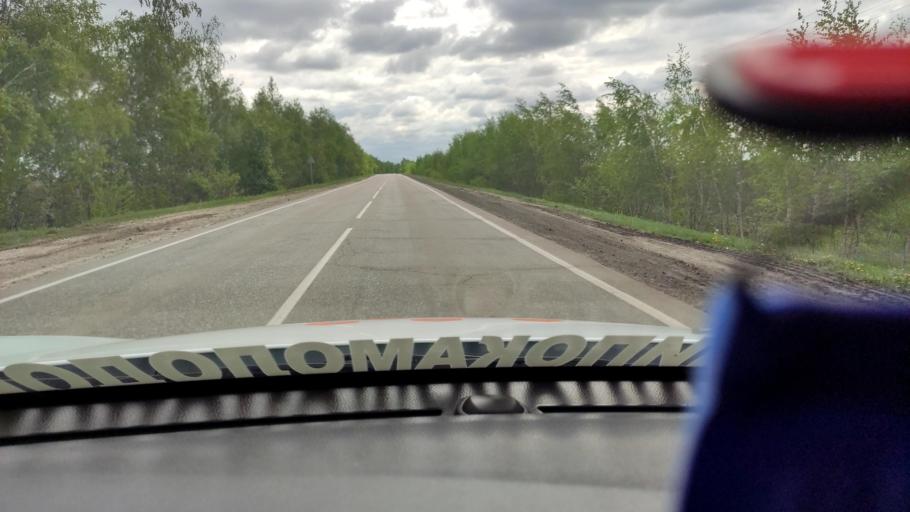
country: RU
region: Voronezj
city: Liski
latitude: 50.7982
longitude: 39.3537
